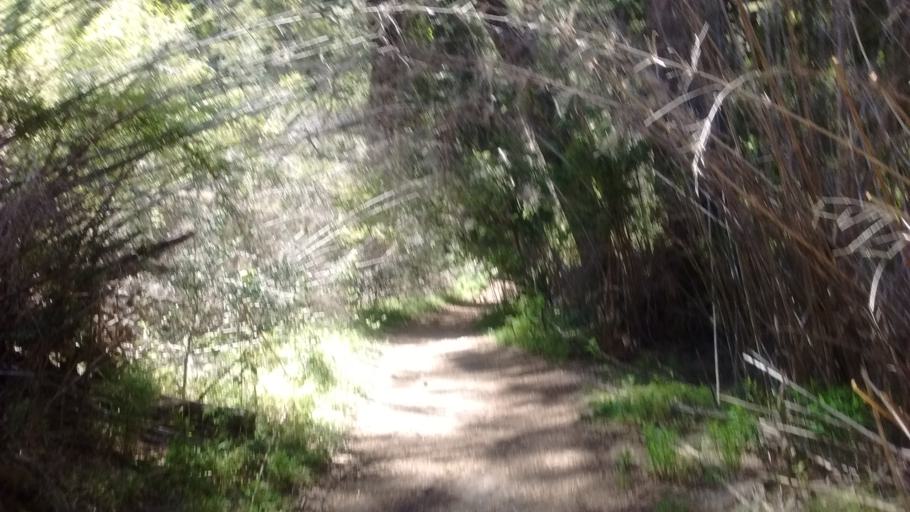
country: AR
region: Rio Negro
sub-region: Departamento de Bariloche
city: San Carlos de Bariloche
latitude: -41.0544
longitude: -71.5576
